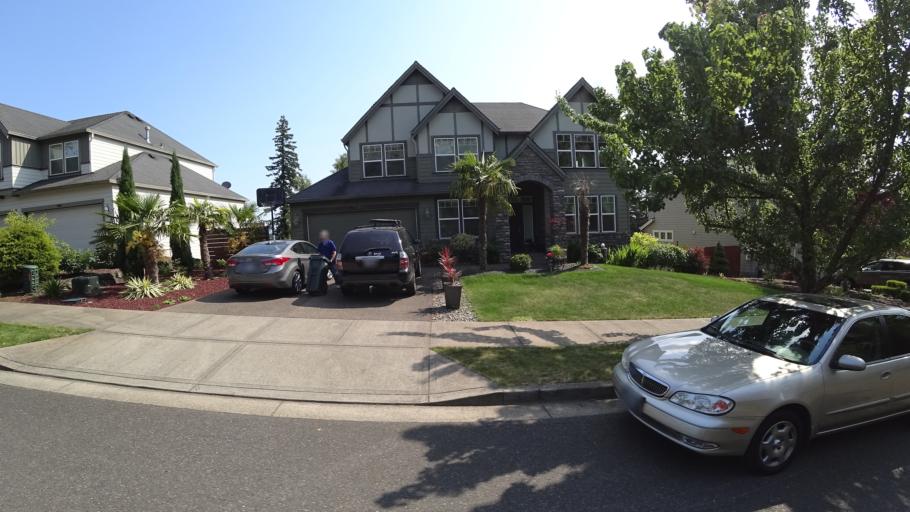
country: US
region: Oregon
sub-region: Clackamas County
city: Happy Valley
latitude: 45.4406
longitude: -122.5495
